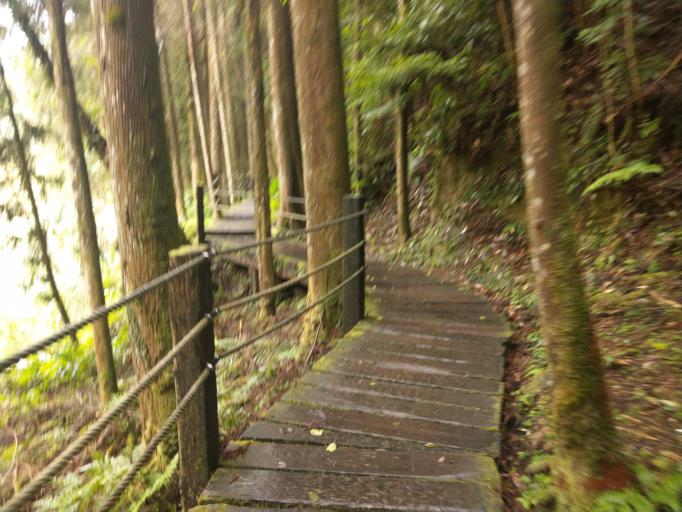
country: TW
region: Taiwan
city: Lugu
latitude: 23.6298
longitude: 120.7964
